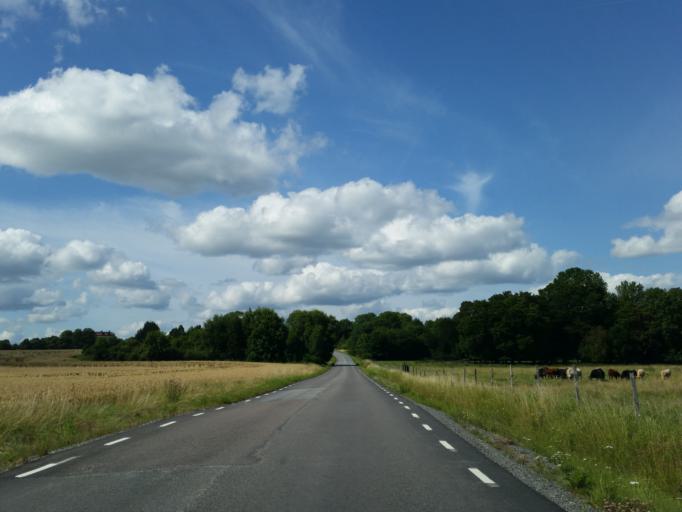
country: SE
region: Stockholm
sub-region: Sodertalje Kommun
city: Pershagen
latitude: 59.0482
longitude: 17.6804
